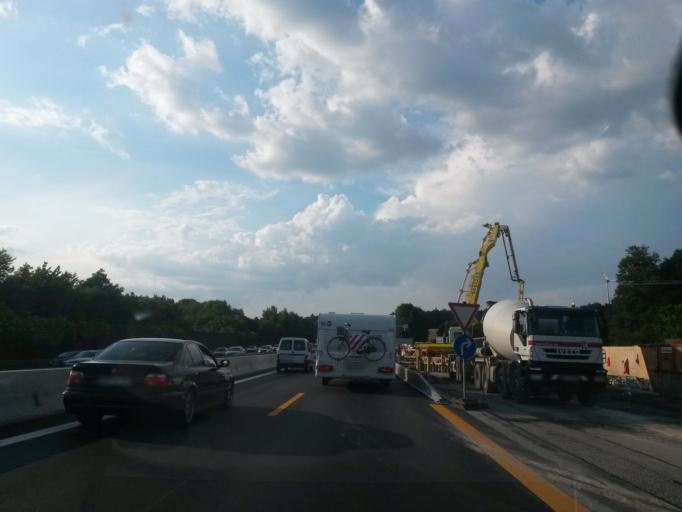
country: DE
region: Bavaria
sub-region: Upper Bavaria
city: Allershausen
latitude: 48.4619
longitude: 11.5897
